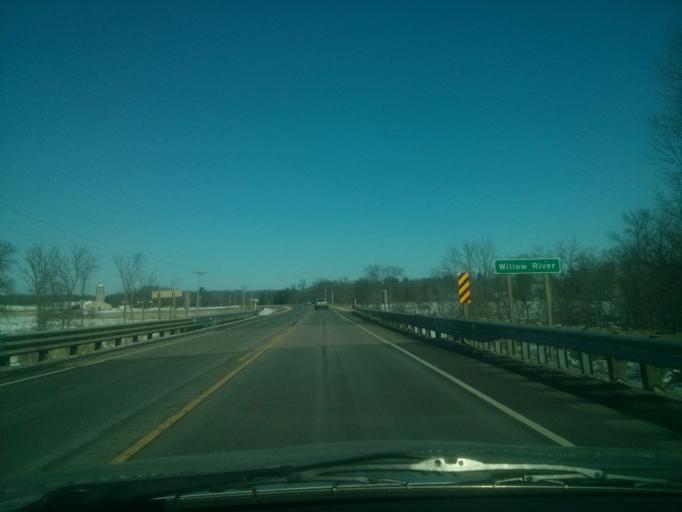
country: US
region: Wisconsin
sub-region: Polk County
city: Clear Lake
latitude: 45.1674
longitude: -92.2827
